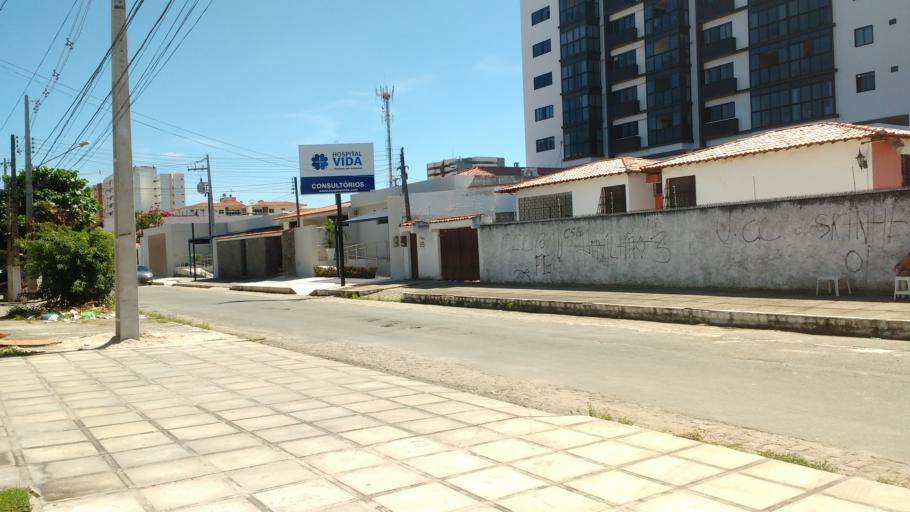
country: BR
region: Alagoas
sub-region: Maceio
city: Maceio
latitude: -9.6542
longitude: -35.7041
